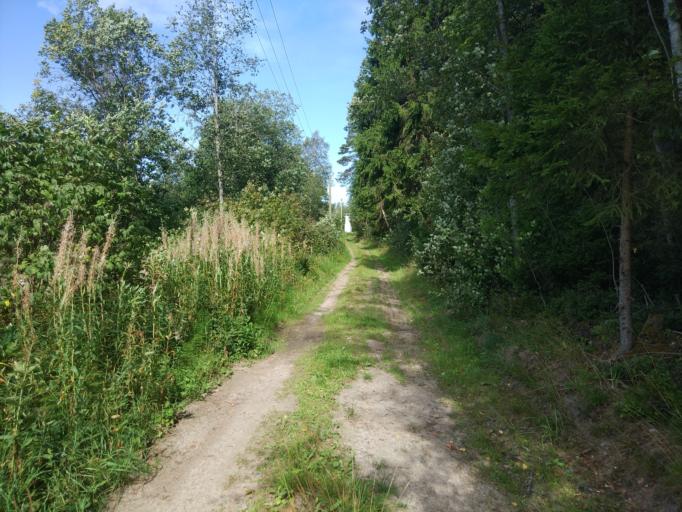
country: RU
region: Leningrad
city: Kamennogorsk
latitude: 61.0470
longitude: 29.4666
